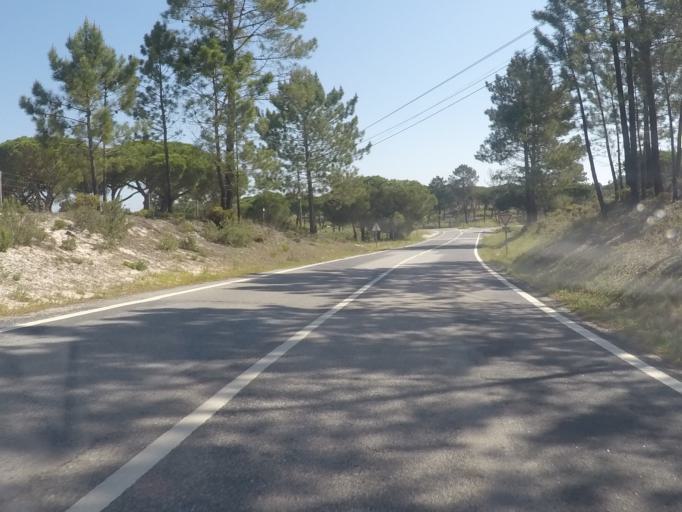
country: PT
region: Setubal
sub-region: Grandola
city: Grandola
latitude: 38.2962
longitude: -8.7261
